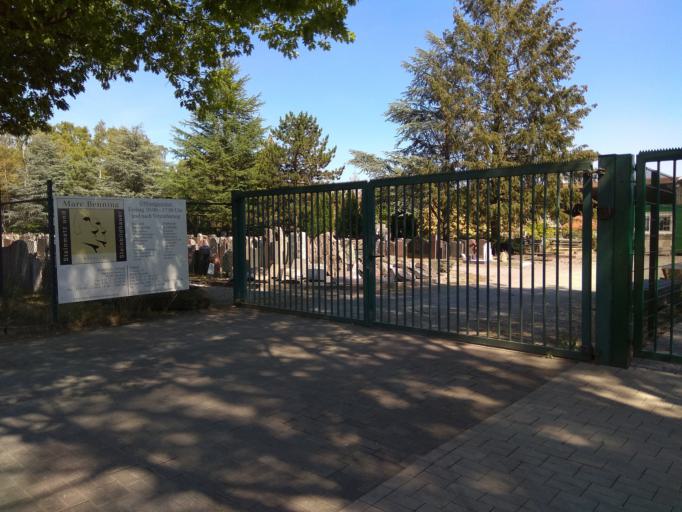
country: DE
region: North Rhine-Westphalia
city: Dorsten
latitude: 51.7172
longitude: 7.0033
